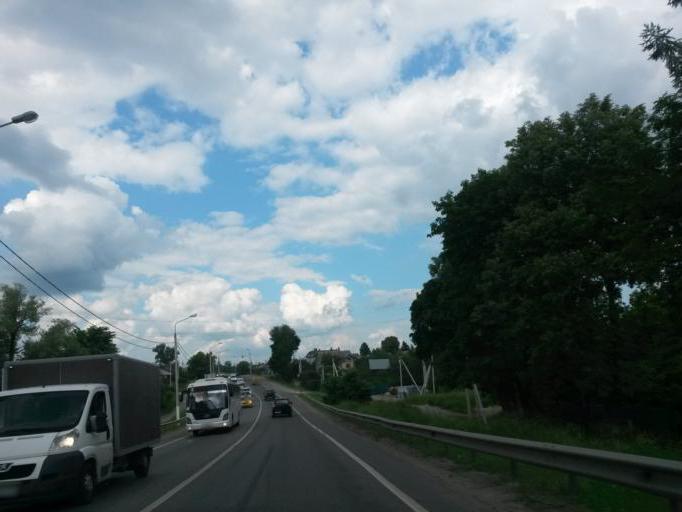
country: RU
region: Moskovskaya
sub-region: Chekhovskiy Rayon
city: Chekhov
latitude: 55.1811
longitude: 37.4899
